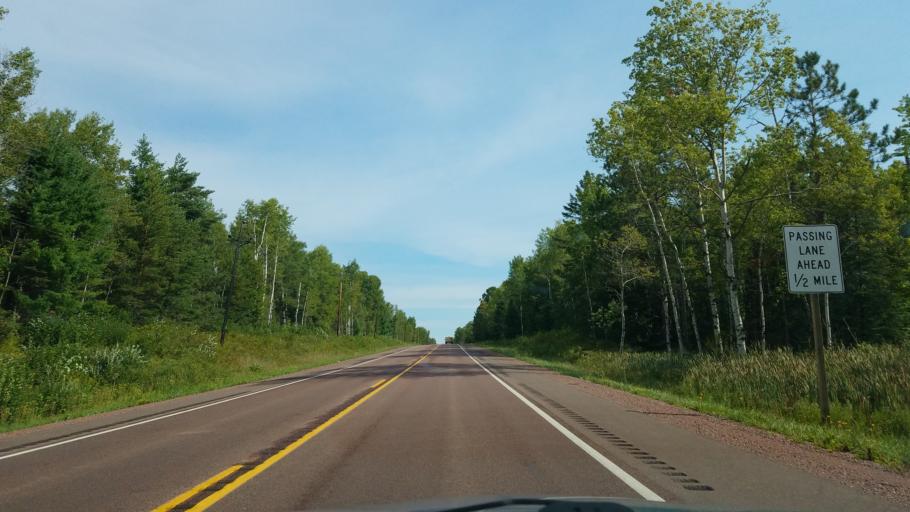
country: US
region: Wisconsin
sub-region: Ashland County
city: Ashland
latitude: 46.6102
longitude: -90.9438
